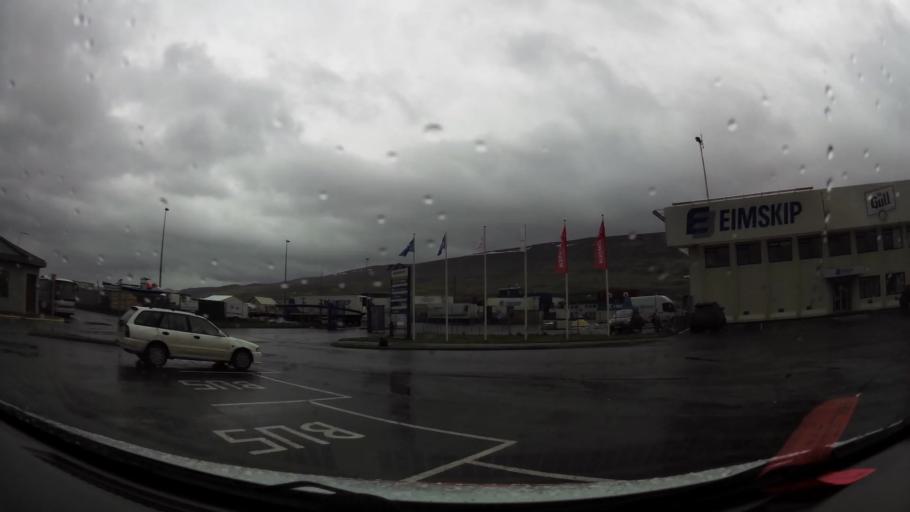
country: IS
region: Northeast
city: Akureyri
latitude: 65.6856
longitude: -18.0790
